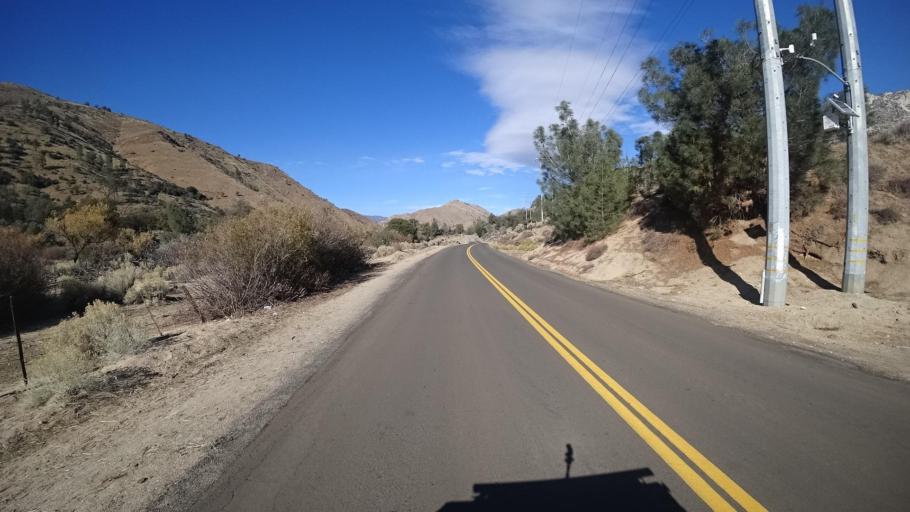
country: US
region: California
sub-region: Kern County
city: Bodfish
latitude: 35.5292
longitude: -118.5122
